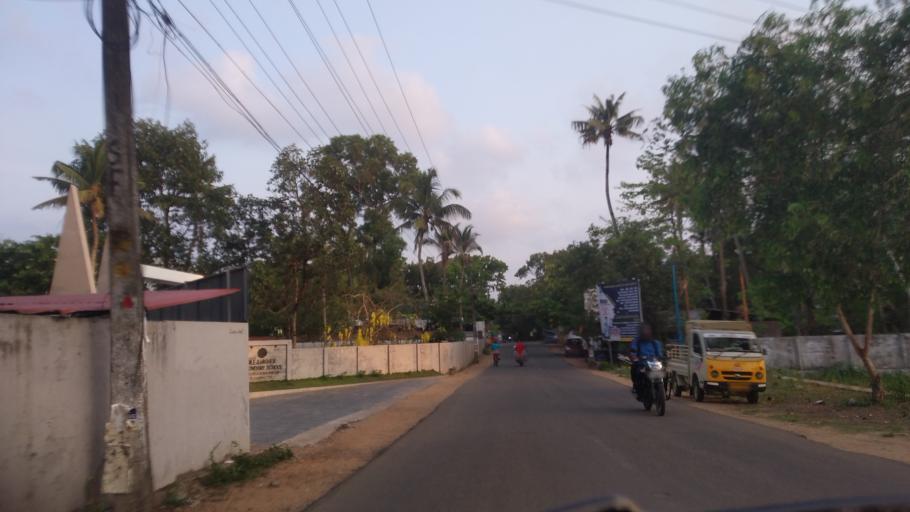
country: IN
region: Kerala
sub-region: Thrissur District
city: Kodungallur
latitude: 10.2661
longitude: 76.1424
